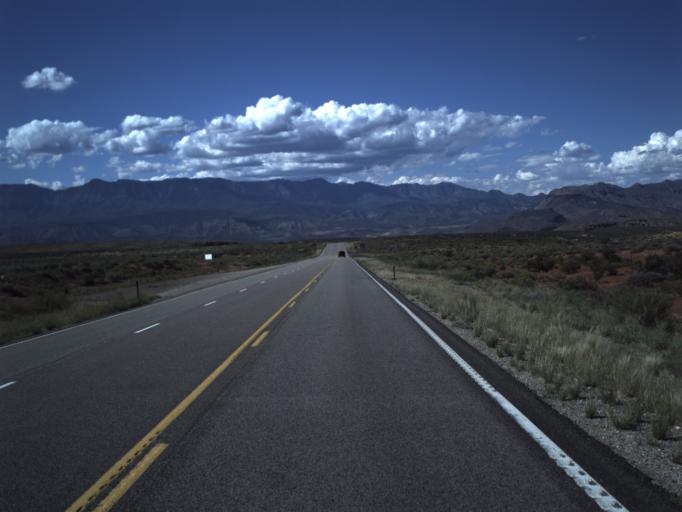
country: US
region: Utah
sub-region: Washington County
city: Hurricane
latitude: 37.1530
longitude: -113.2576
